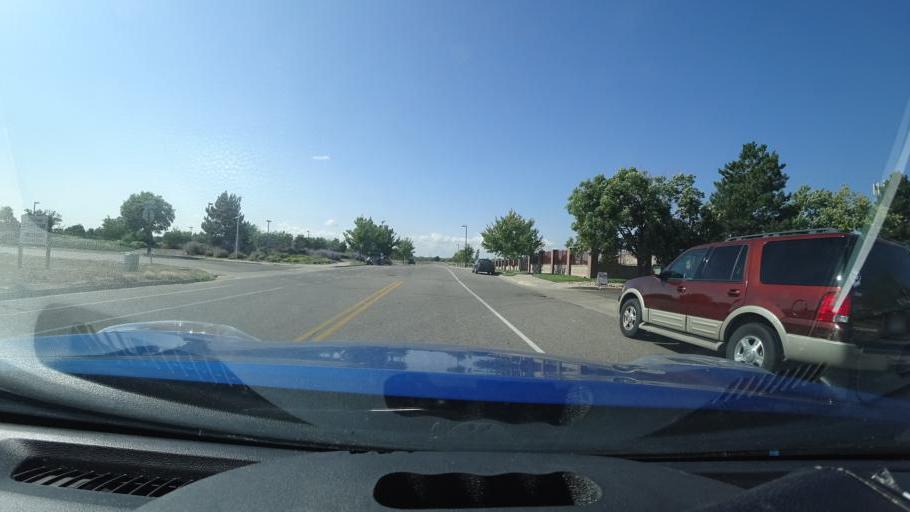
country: US
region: Colorado
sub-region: Adams County
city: Aurora
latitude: 39.7224
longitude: -104.8006
